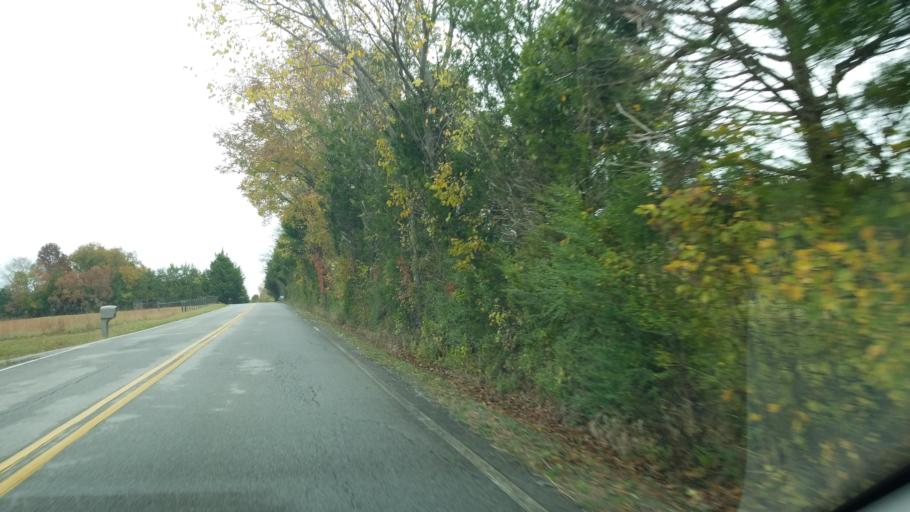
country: US
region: Tennessee
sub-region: Bradley County
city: Hopewell
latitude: 35.2477
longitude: -84.9840
